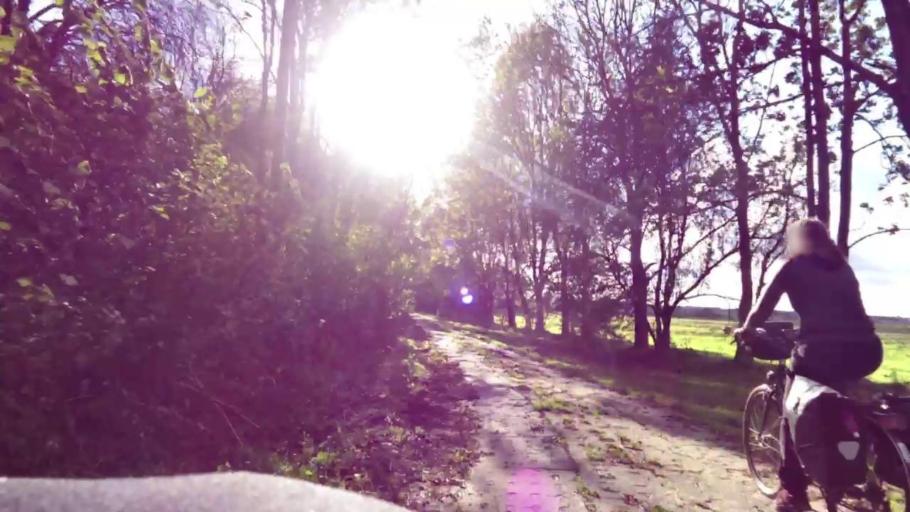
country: PL
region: West Pomeranian Voivodeship
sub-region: Powiat bialogardzki
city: Bialogard
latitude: 54.0152
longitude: 16.0563
